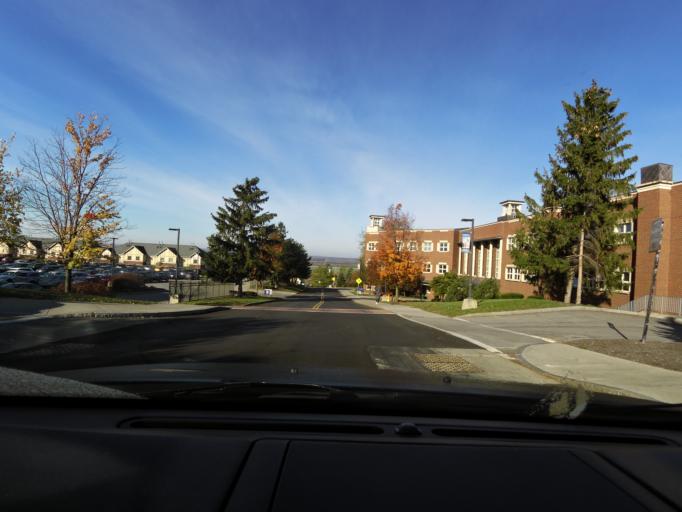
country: US
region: New York
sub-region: Livingston County
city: Geneseo
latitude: 42.7949
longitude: -77.8204
